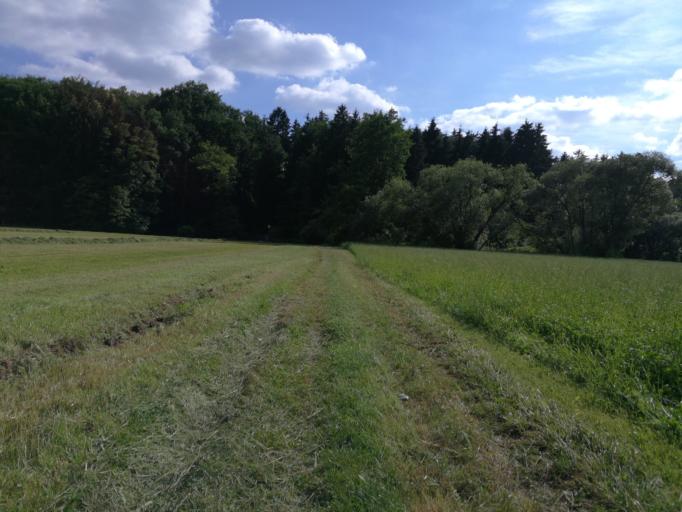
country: DE
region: Bavaria
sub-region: Regierungsbezirk Mittelfranken
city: Obermichelbach
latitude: 49.5075
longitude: 10.9253
